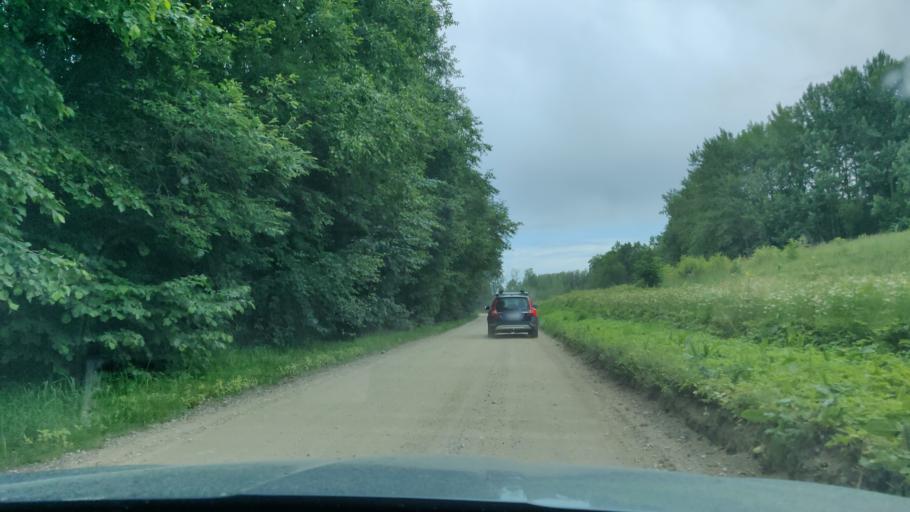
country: EE
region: Vorumaa
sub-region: Antsla vald
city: Vana-Antsla
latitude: 58.0356
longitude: 26.5545
